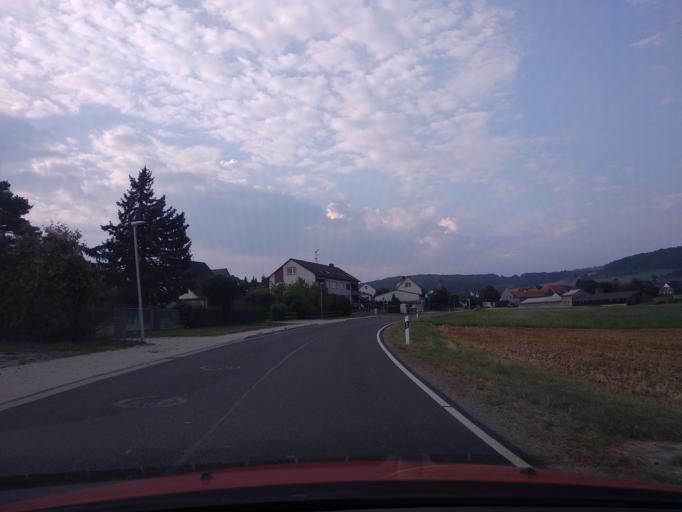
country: DE
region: Hesse
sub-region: Regierungsbezirk Kassel
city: Calden
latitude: 51.3884
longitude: 9.3644
